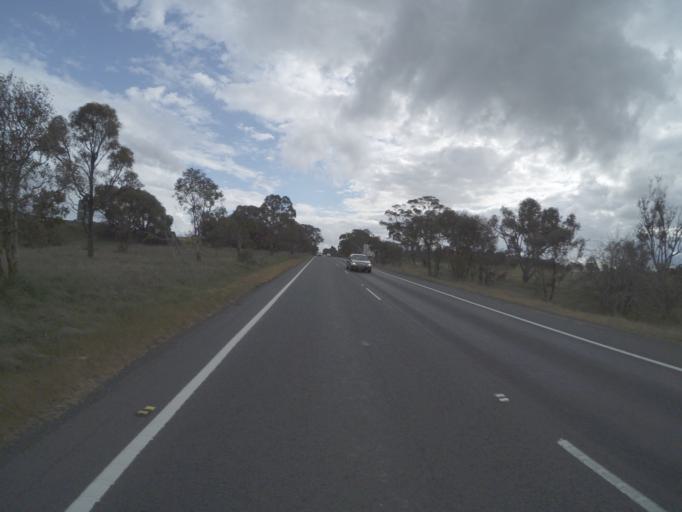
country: AU
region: New South Wales
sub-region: Goulburn Mulwaree
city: Goulburn
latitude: -34.7359
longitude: 149.7892
